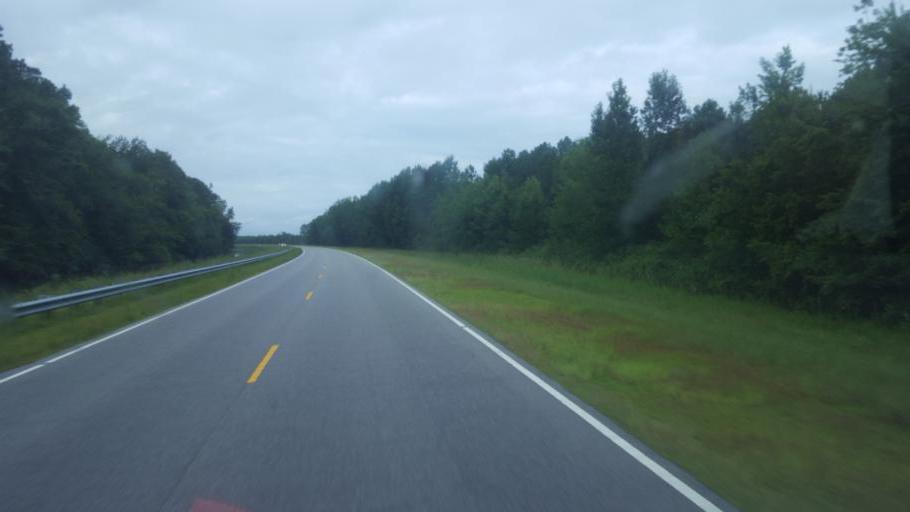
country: US
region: North Carolina
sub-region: Tyrrell County
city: Columbia
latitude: 35.9317
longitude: -76.1478
